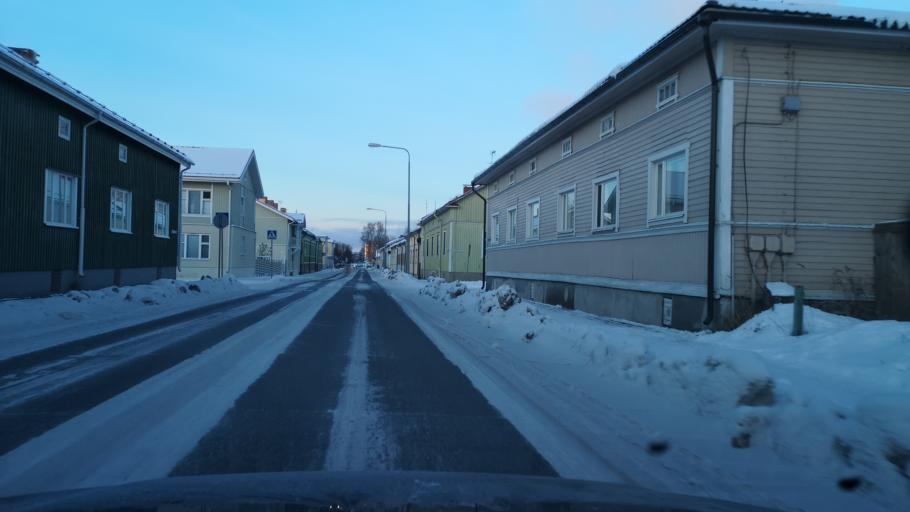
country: FI
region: Satakunta
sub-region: Pori
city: Pori
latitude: 61.4820
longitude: 21.8065
